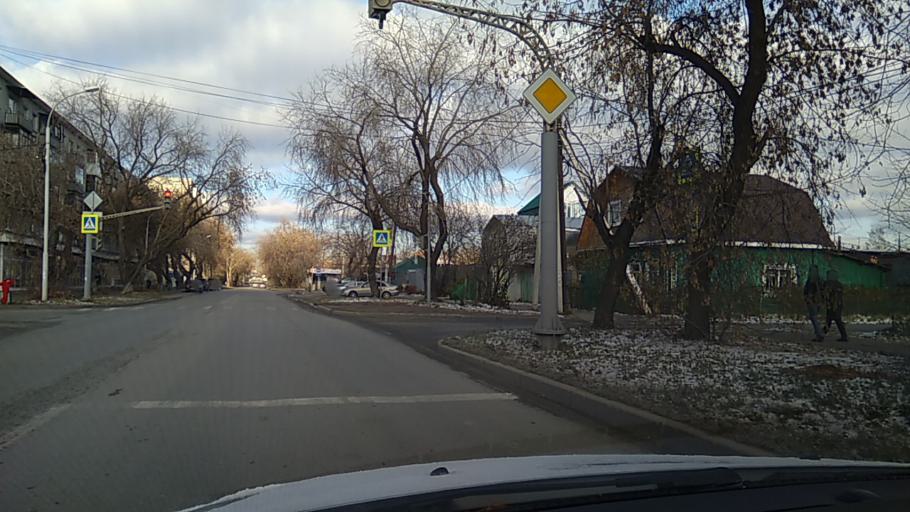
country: RU
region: Sverdlovsk
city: Sovkhoznyy
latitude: 56.7499
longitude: 60.6197
